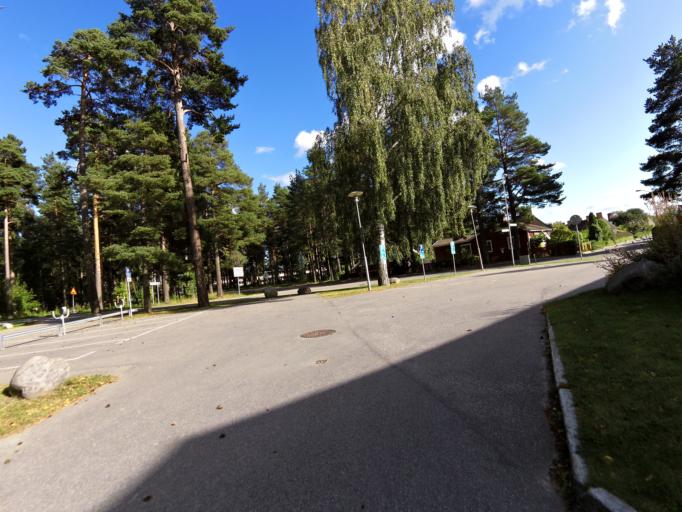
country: SE
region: Gaevleborg
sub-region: Gavle Kommun
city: Gavle
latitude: 60.7061
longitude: 17.1633
